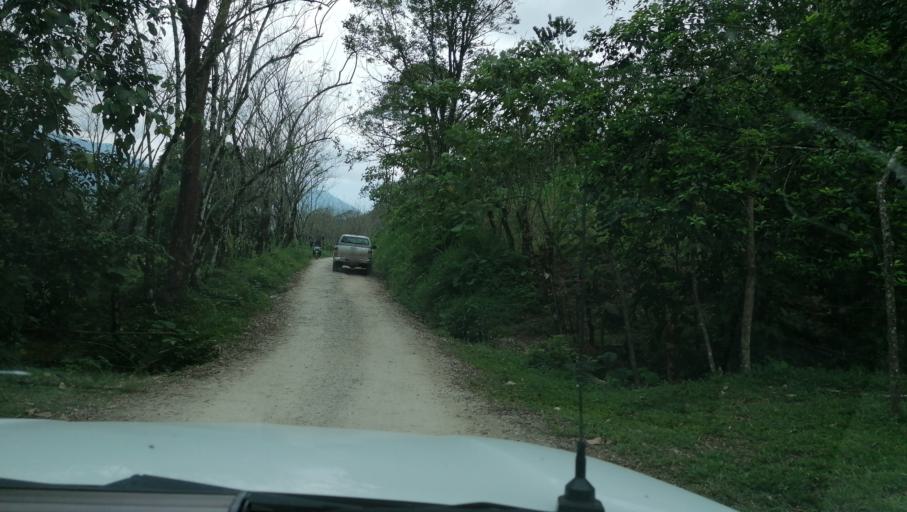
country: MX
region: Chiapas
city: Ocotepec
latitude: 17.2743
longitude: -93.2240
